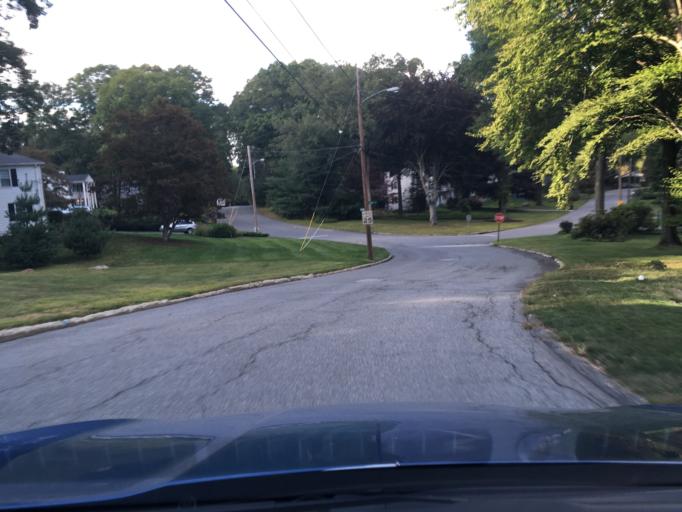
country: US
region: Rhode Island
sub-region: Kent County
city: East Greenwich
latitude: 41.6509
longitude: -71.4863
